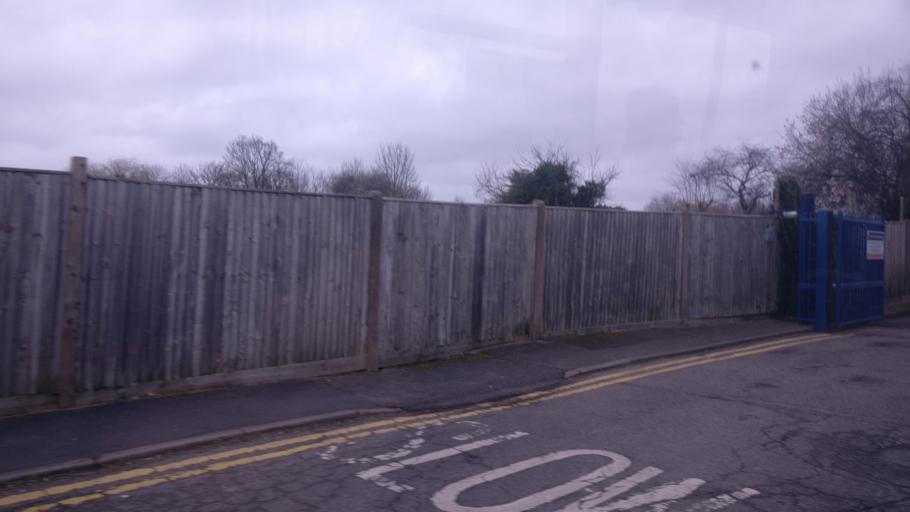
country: GB
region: England
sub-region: Surrey
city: Chertsey
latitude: 51.4084
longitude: -0.5033
